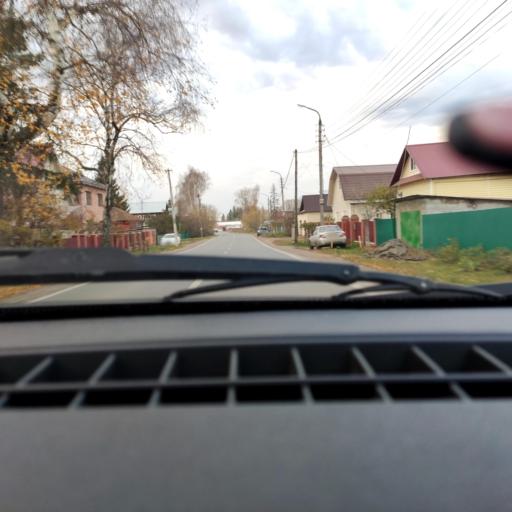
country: RU
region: Bashkortostan
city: Iglino
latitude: 54.8293
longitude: 56.1879
